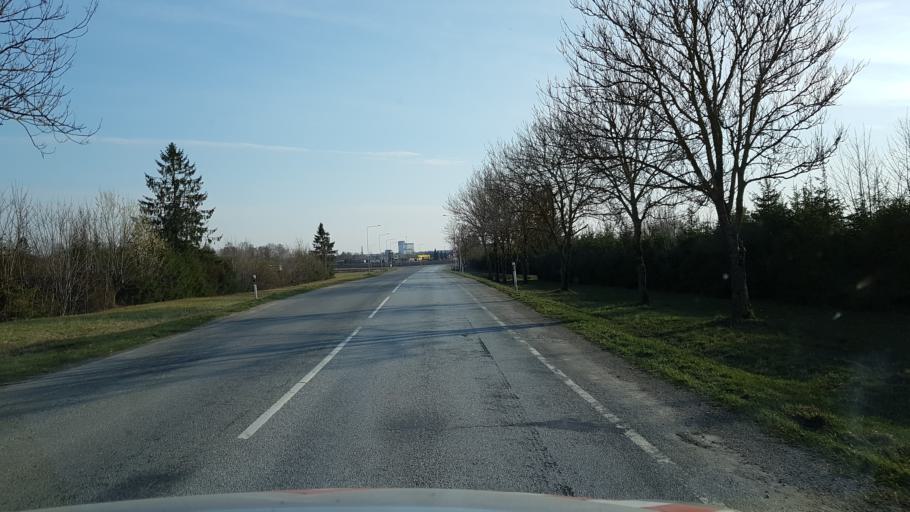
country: EE
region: Laeaene-Virumaa
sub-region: Rakvere linn
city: Rakvere
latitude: 59.3753
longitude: 26.3882
